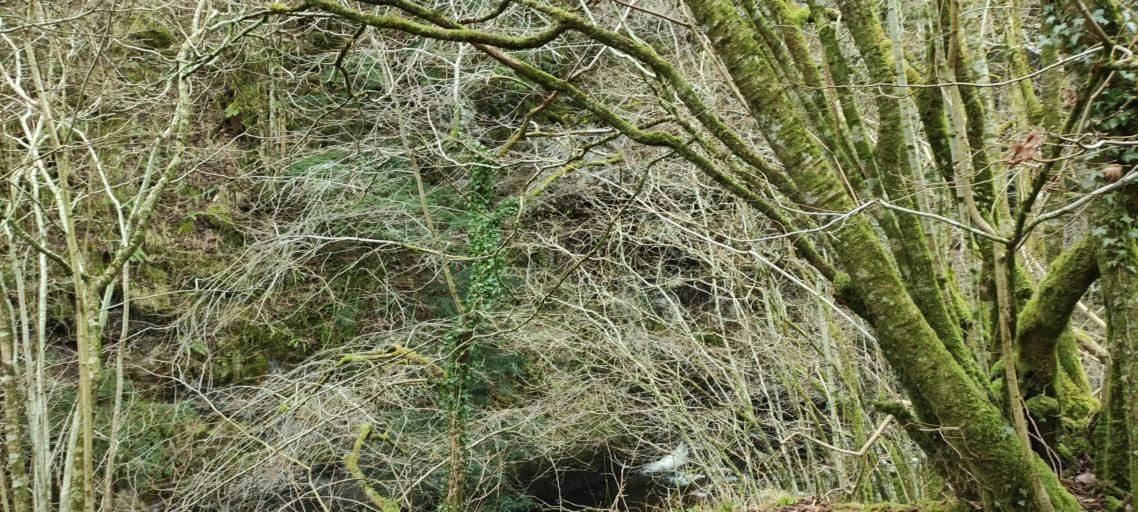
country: GB
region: England
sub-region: North Yorkshire
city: Ingleton
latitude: 54.1671
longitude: -2.4692
